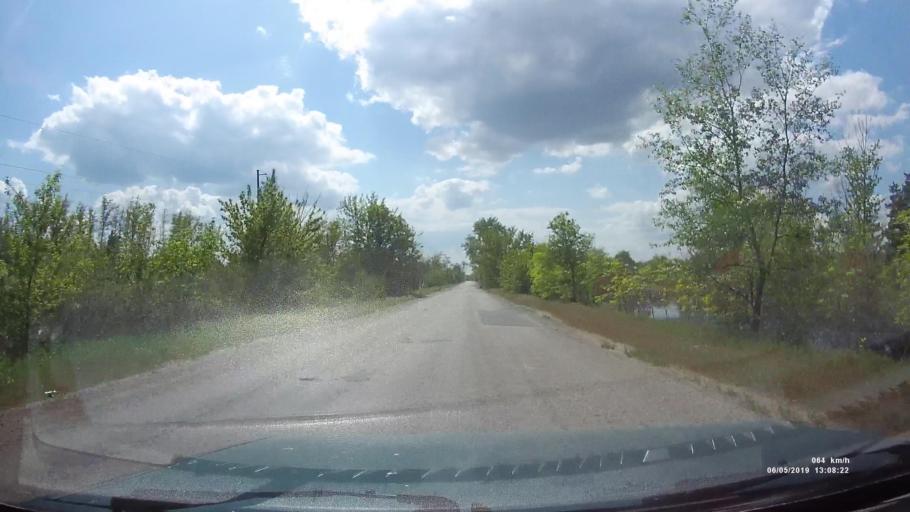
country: RU
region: Rostov
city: Ust'-Donetskiy
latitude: 47.7761
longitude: 40.9961
